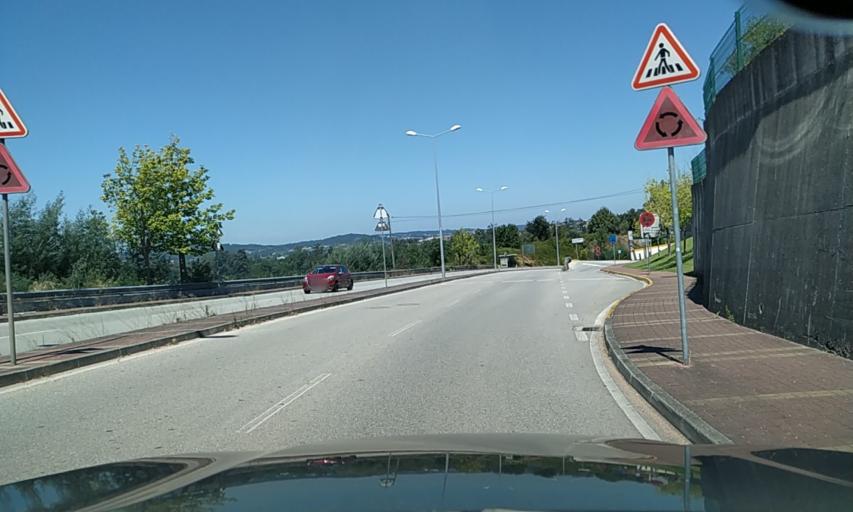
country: PT
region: Coimbra
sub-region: Coimbra
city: Coimbra
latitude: 40.2112
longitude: -8.4453
